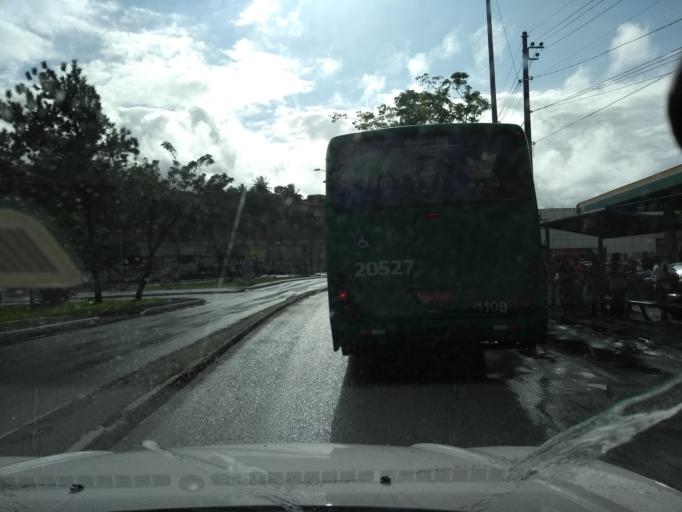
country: BR
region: Bahia
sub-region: Salvador
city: Salvador
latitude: -12.9664
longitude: -38.4929
